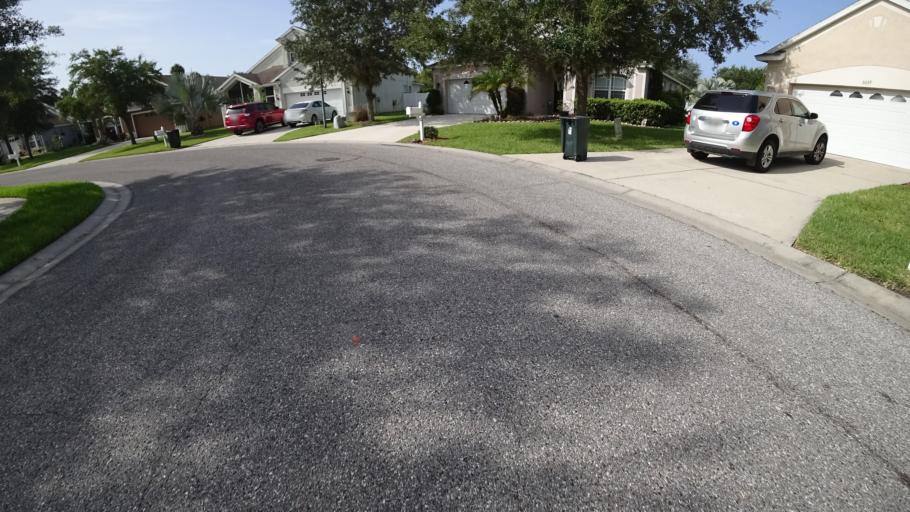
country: US
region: Florida
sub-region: Manatee County
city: Ellenton
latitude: 27.5525
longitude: -82.4965
